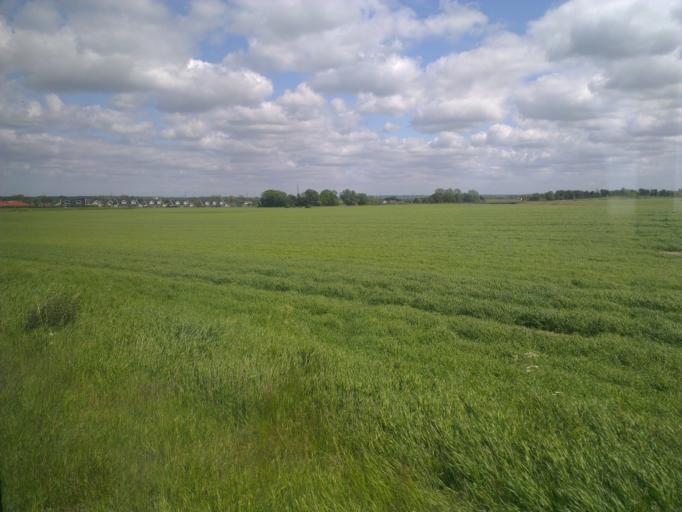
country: DK
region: Capital Region
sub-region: Frederikssund Kommune
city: Slangerup
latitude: 55.8774
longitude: 12.1930
